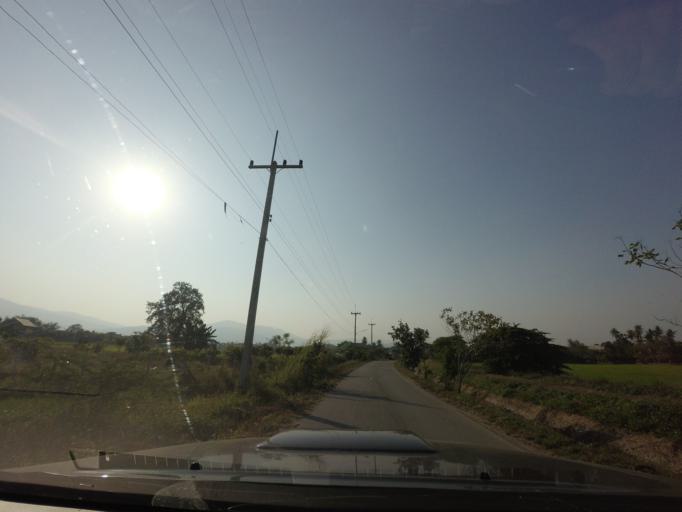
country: TH
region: Chiang Mai
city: San Sai
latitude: 18.9409
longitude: 98.9530
